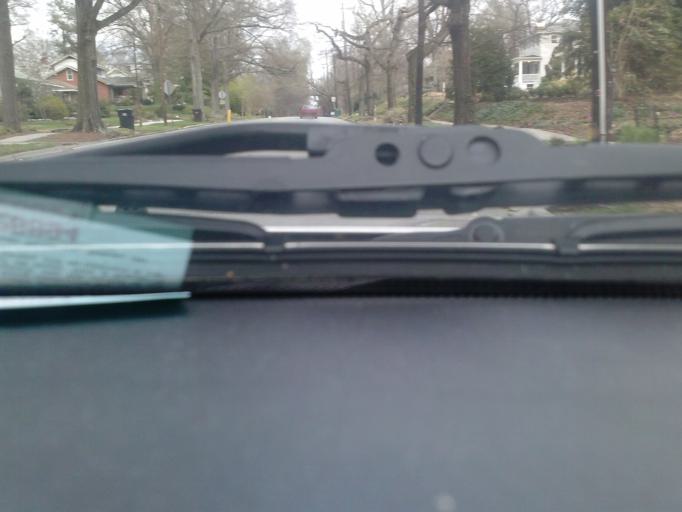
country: US
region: North Carolina
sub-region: Durham County
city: Durham
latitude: 36.0175
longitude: -78.9274
